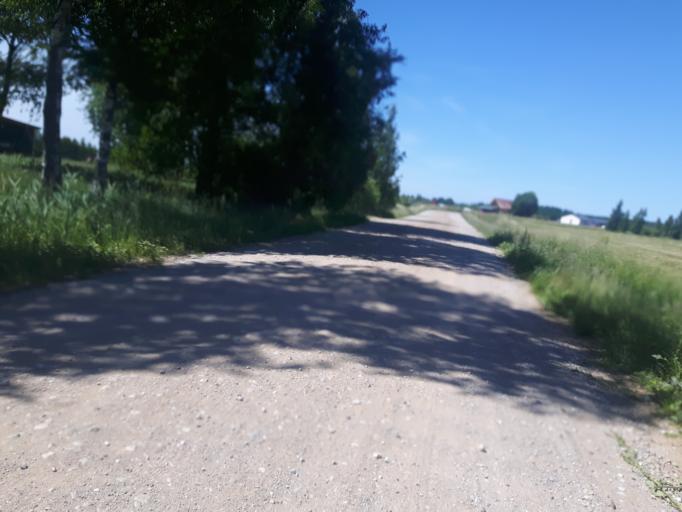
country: LV
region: Grobina
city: Grobina
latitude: 56.5284
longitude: 21.1324
